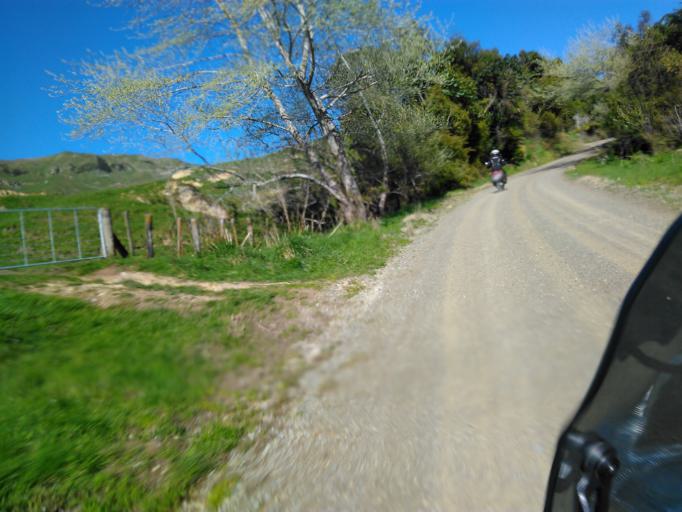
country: NZ
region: Gisborne
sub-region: Gisborne District
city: Gisborne
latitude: -38.3733
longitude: 177.6080
